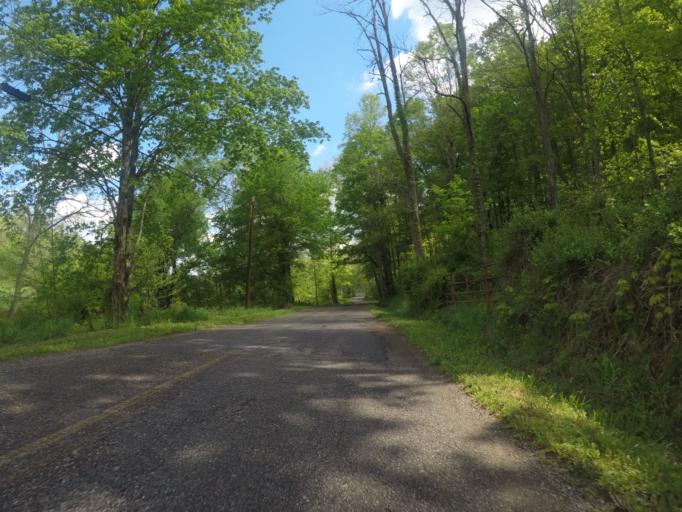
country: US
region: West Virginia
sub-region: Cabell County
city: Huntington
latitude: 38.5101
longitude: -82.4410
